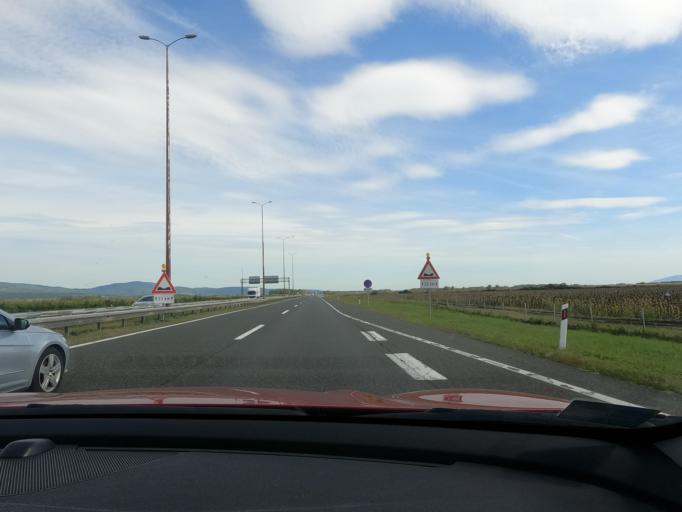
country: HR
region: Brodsko-Posavska
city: Ljupina
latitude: 45.2276
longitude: 17.4148
